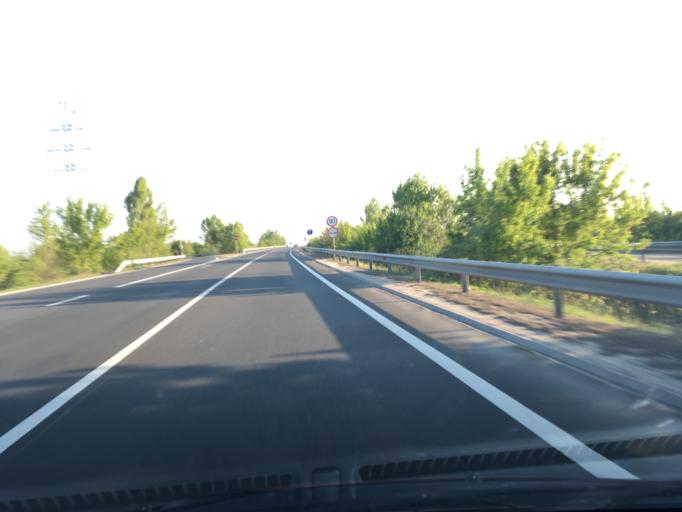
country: HU
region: Pest
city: Szod
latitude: 47.7499
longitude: 19.1779
